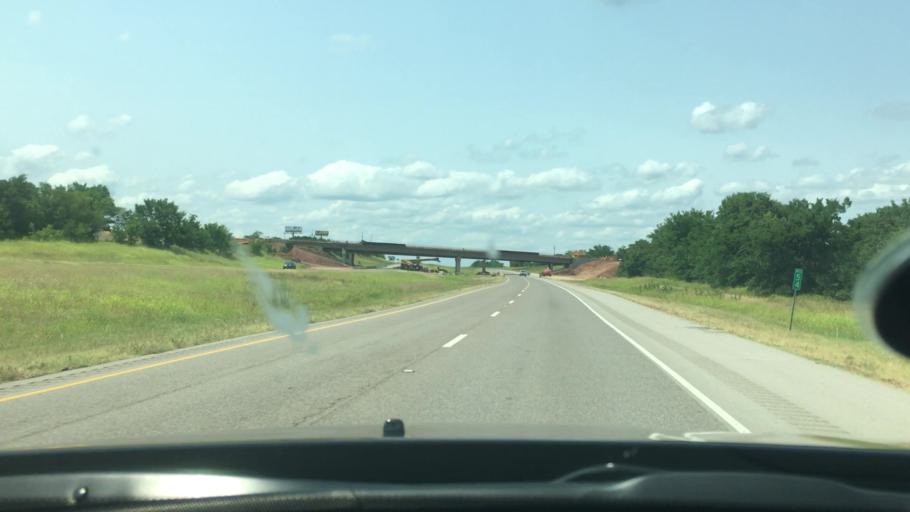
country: US
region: Oklahoma
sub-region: Murray County
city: Davis
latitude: 34.4854
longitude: -97.1594
